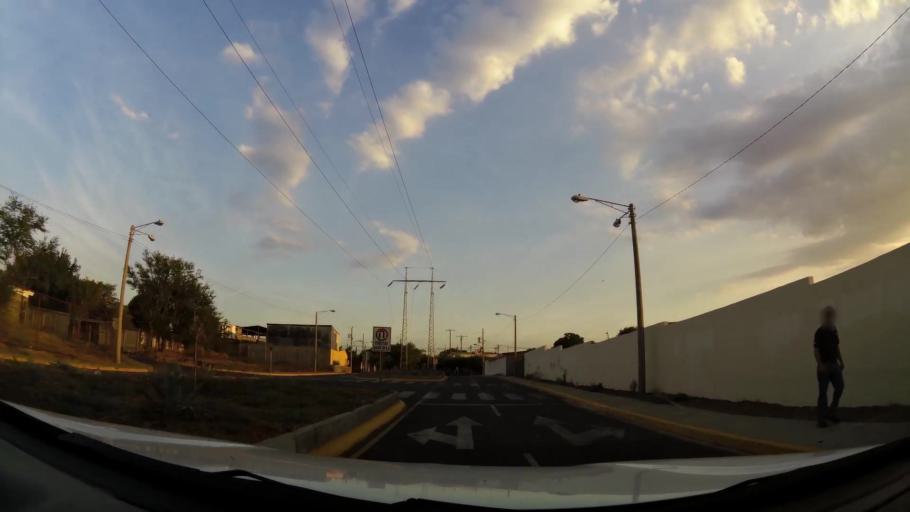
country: NI
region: Managua
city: Managua
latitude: 12.1498
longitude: -86.2344
